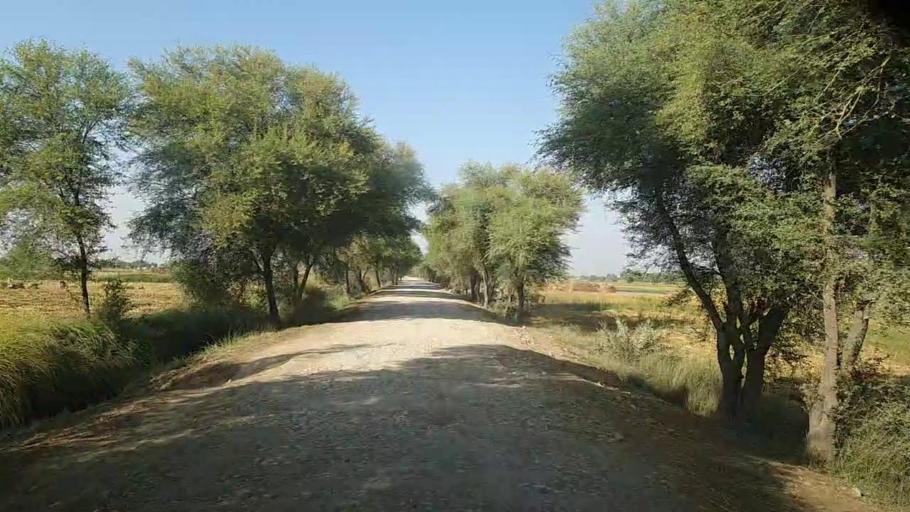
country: PK
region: Sindh
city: Tangwani
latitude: 28.2814
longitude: 68.9843
